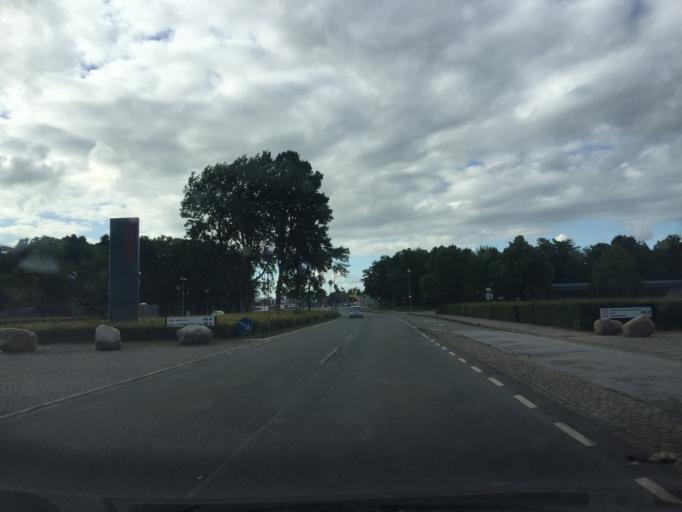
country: DK
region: Capital Region
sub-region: Albertslund Kommune
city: Albertslund
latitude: 55.6613
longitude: 12.3623
